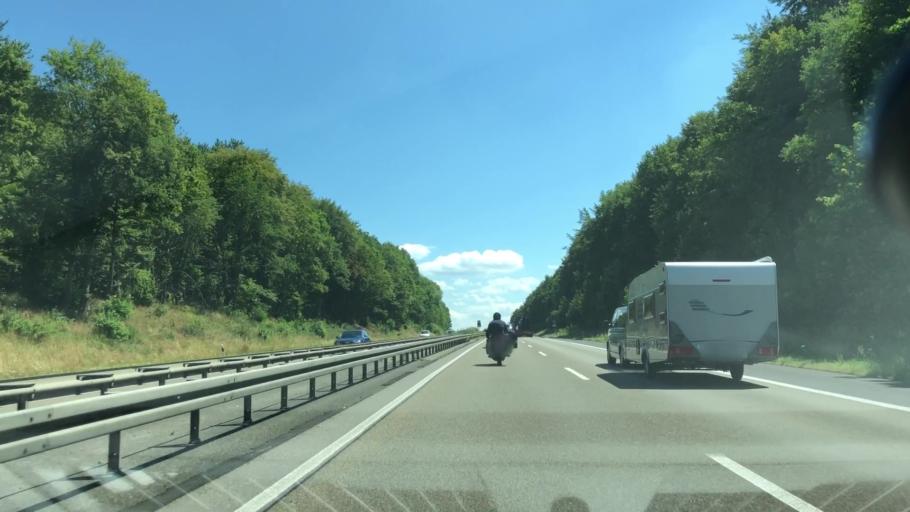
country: DE
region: Hesse
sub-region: Regierungsbezirk Kassel
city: Martinhagen
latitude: 51.3009
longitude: 9.3246
